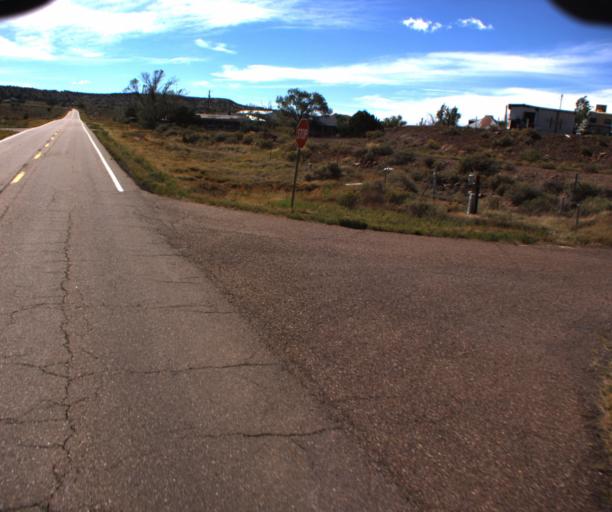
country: US
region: Arizona
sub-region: Apache County
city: Saint Johns
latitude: 34.4737
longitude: -109.6058
